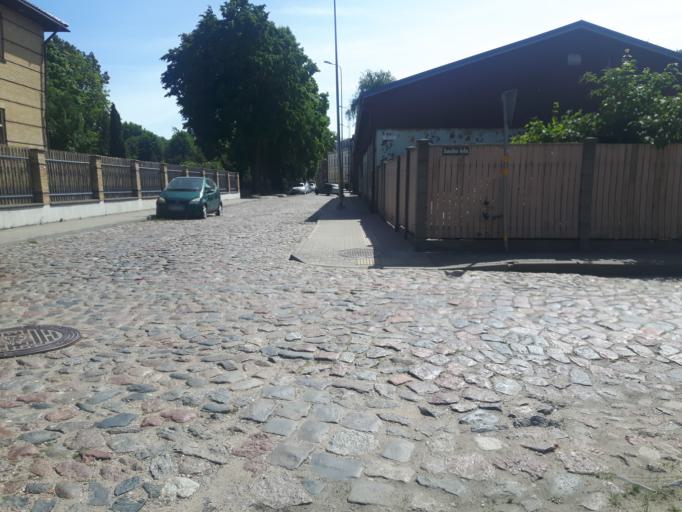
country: LV
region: Liepaja
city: Liepaja
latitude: 56.5116
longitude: 21.0012
